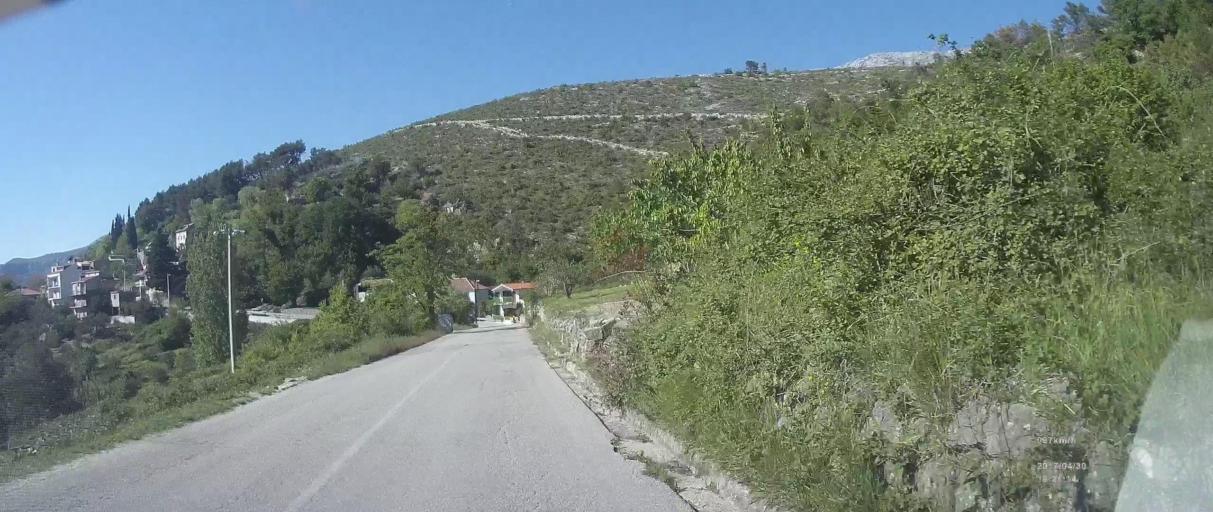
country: HR
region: Splitsko-Dalmatinska
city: Srinjine
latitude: 43.5045
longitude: 16.5990
